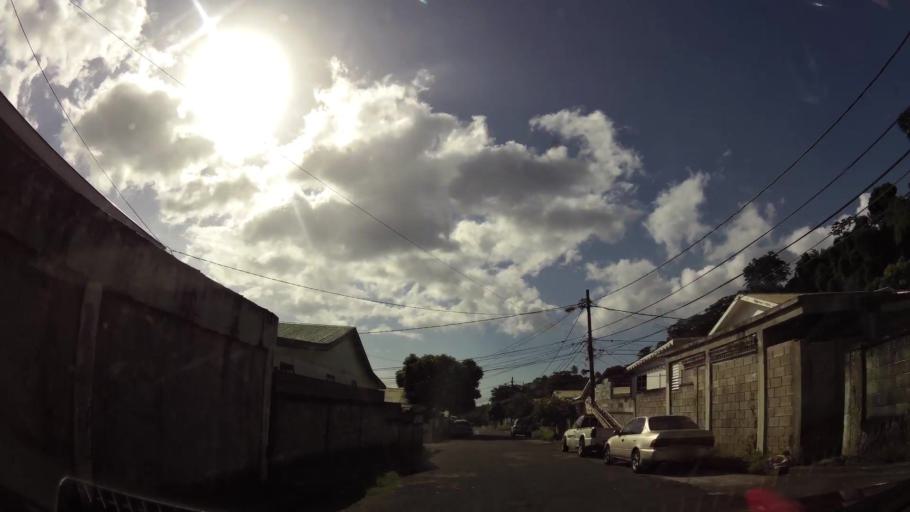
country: DM
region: Saint George
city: Roseau
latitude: 15.3039
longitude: -61.3787
